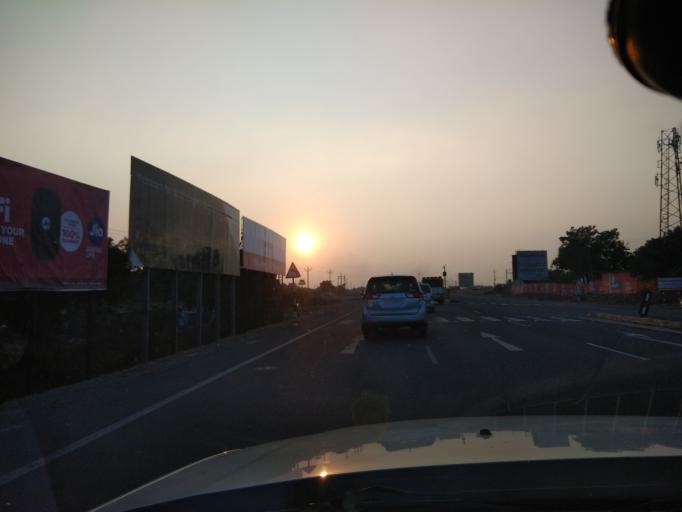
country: IN
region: Gujarat
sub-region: Jamnagar
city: Jamnagar
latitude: 22.4504
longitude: 70.0128
